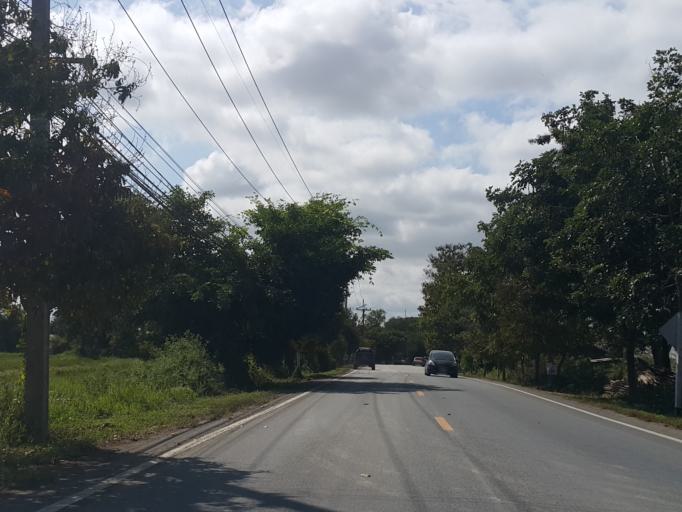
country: TH
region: Lamphun
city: Ban Thi
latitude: 18.6764
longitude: 99.1471
